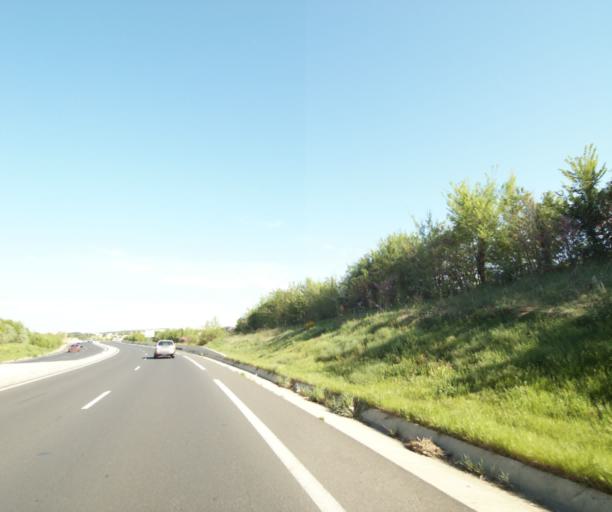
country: FR
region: Languedoc-Roussillon
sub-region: Departement de l'Herault
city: Le Cres
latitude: 43.6346
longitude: 3.9344
